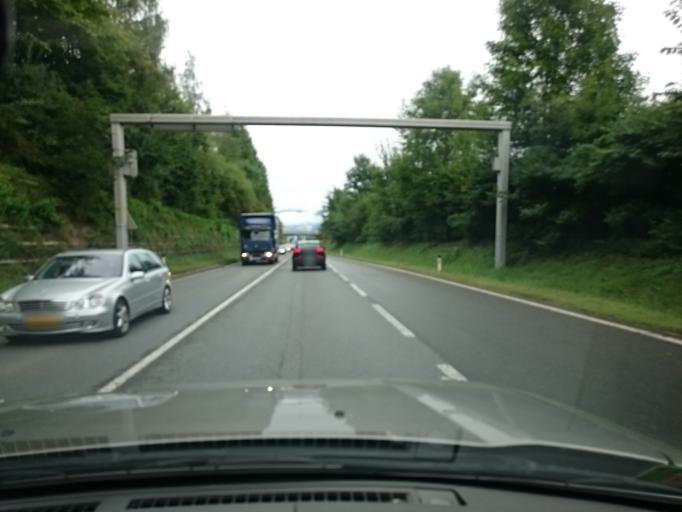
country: AT
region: Salzburg
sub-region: Politischer Bezirk Zell am See
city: Maishofen
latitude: 47.3474
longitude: 12.7996
